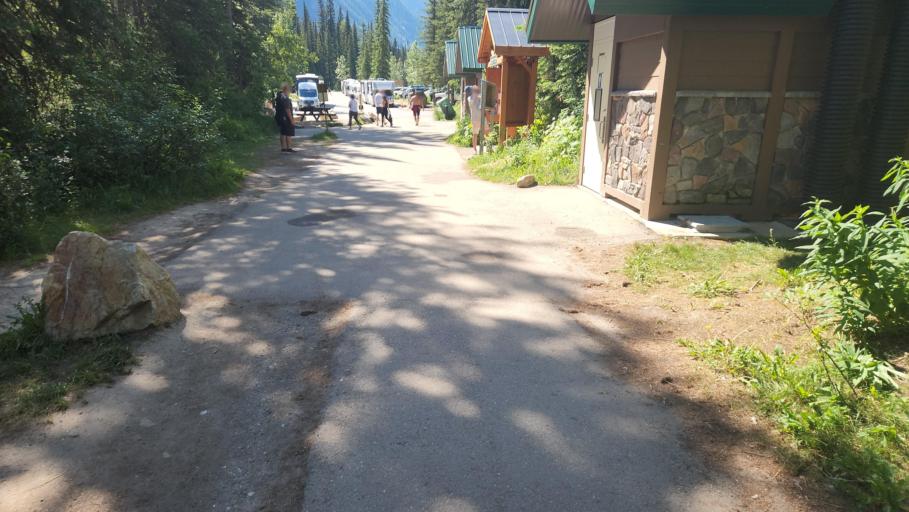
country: CA
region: Alberta
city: Lake Louise
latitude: 51.4399
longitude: -116.5421
